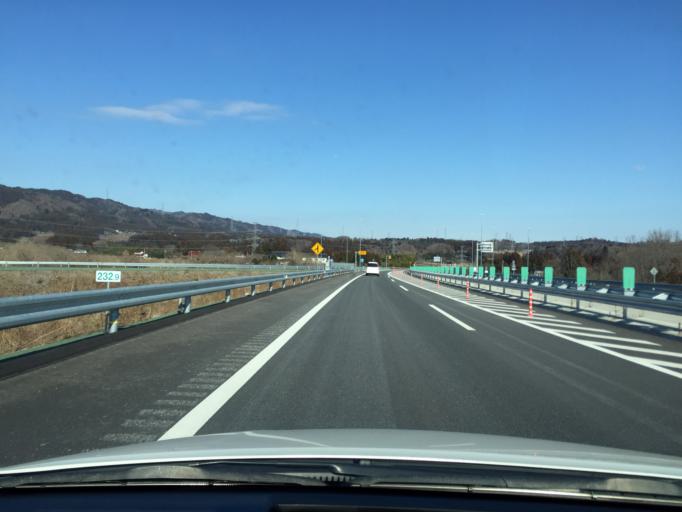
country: JP
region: Fukushima
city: Namie
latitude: 37.4991
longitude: 140.9428
